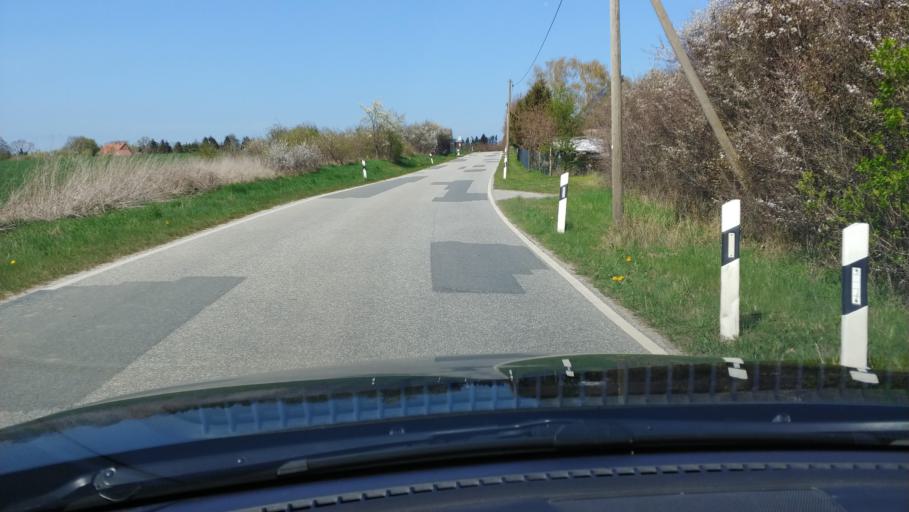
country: DE
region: Mecklenburg-Vorpommern
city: Muhlen Eichsen
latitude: 53.7969
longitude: 11.2660
